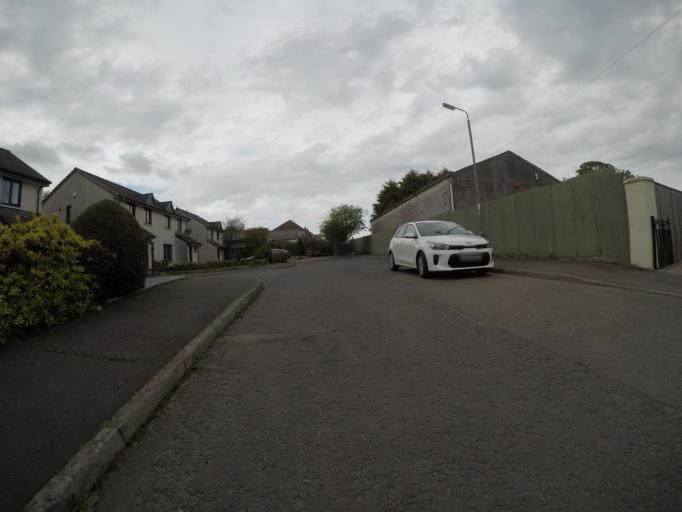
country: GB
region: Scotland
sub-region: East Ayrshire
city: Kilmaurs
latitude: 55.6391
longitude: -4.5298
